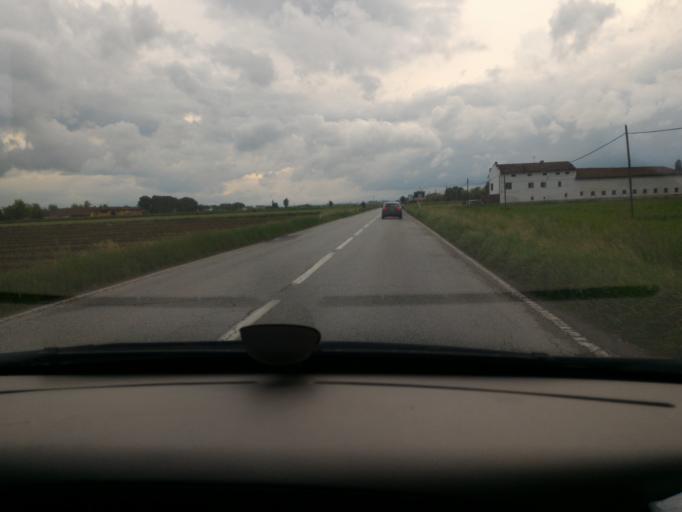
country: IT
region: Piedmont
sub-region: Provincia di Cuneo
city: Savigliano
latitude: 44.6259
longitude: 7.6659
